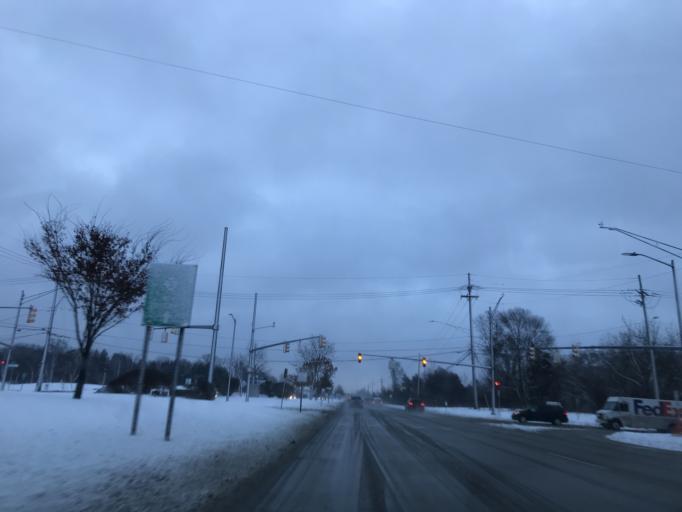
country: US
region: Michigan
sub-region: Oakland County
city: Novi
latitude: 42.4959
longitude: -83.4574
